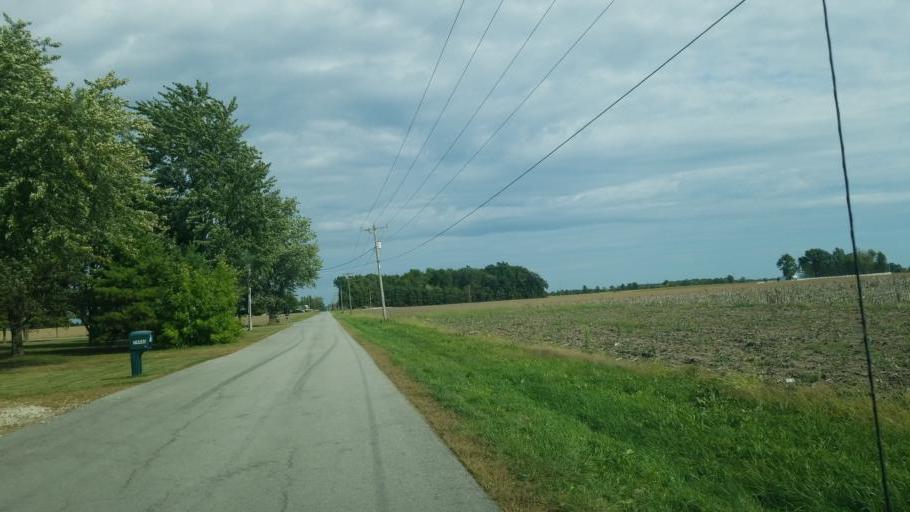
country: US
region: Ohio
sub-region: Hancock County
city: Arlington
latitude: 40.8772
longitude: -83.6068
